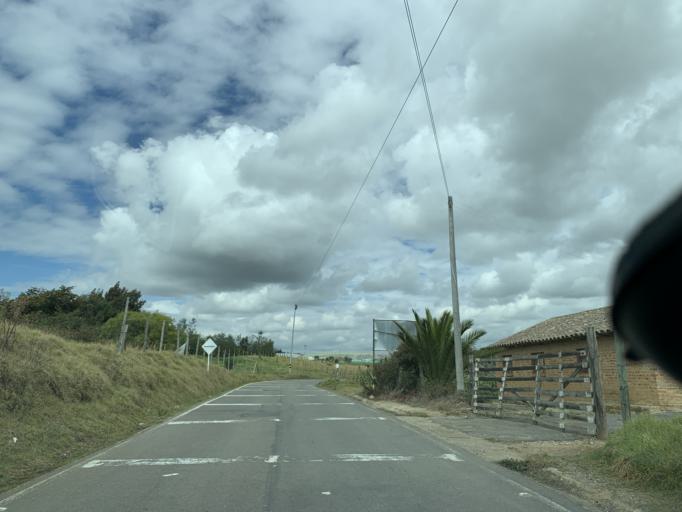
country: CO
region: Boyaca
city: Toca
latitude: 5.5676
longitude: -73.2000
